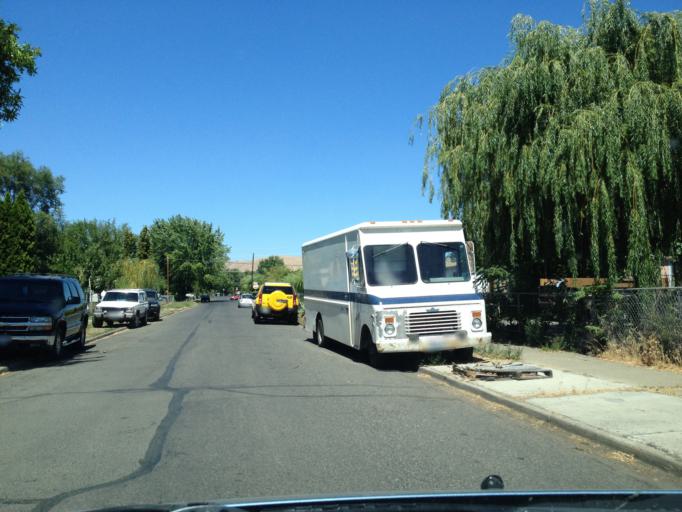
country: US
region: Washington
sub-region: Yakima County
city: Yakima
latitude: 46.5899
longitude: -120.4928
